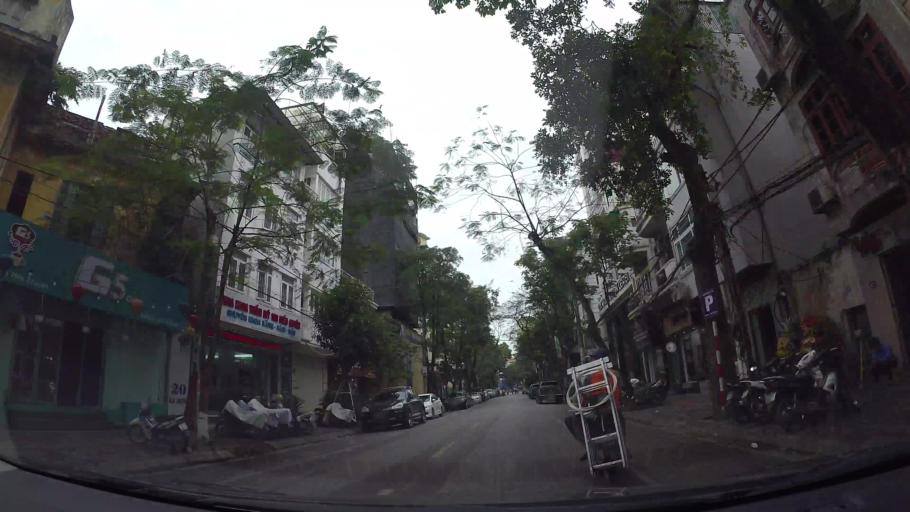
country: VN
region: Ha Noi
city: Hai BaTrung
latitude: 21.0183
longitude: 105.8568
